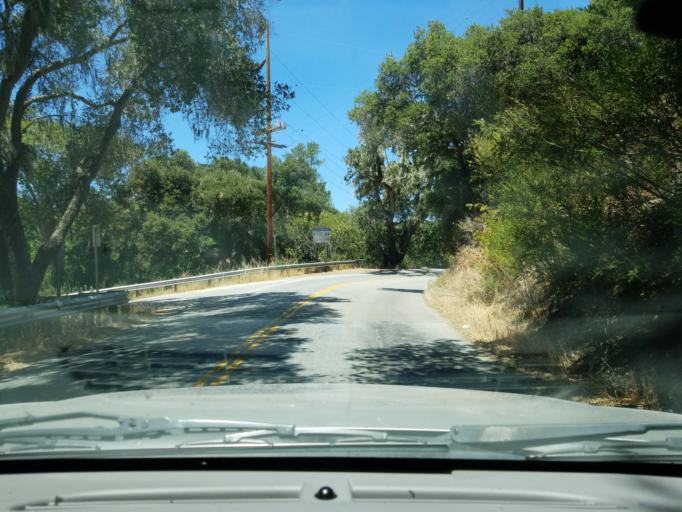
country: US
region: California
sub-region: Monterey County
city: Carmel Valley Village
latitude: 36.4600
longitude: -121.7087
